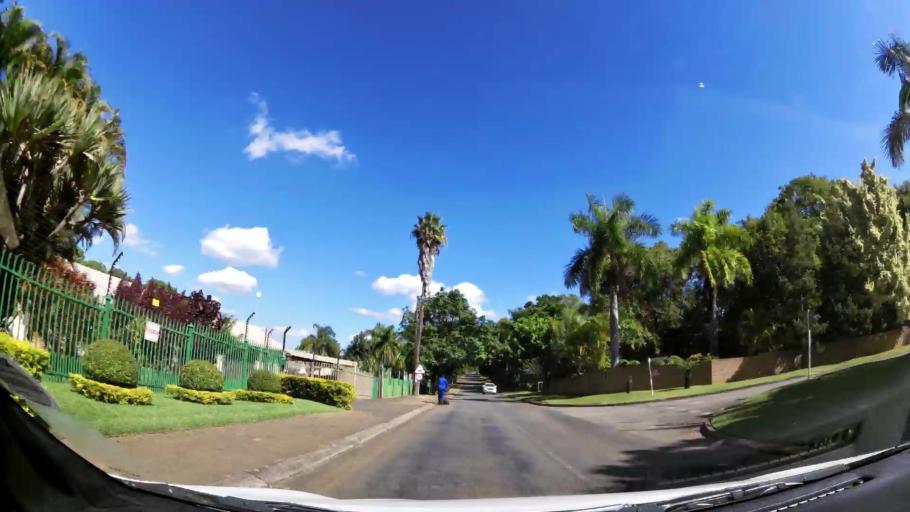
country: ZA
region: Limpopo
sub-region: Mopani District Municipality
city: Tzaneen
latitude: -23.8196
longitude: 30.1495
